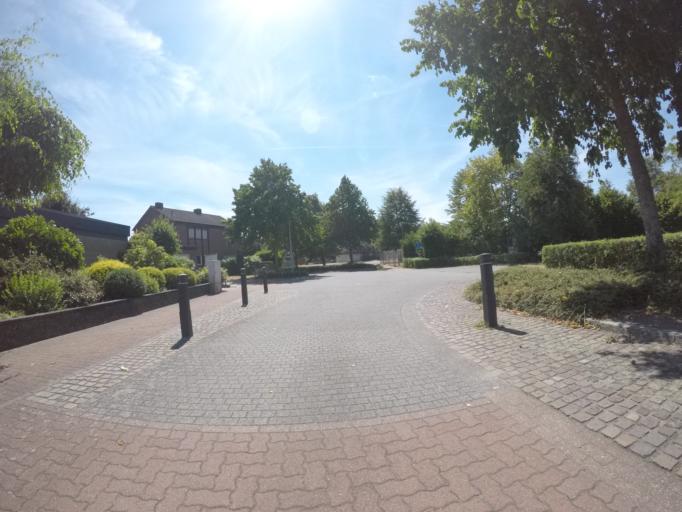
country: DE
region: North Rhine-Westphalia
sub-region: Regierungsbezirk Dusseldorf
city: Bocholt
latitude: 51.8271
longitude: 6.6107
